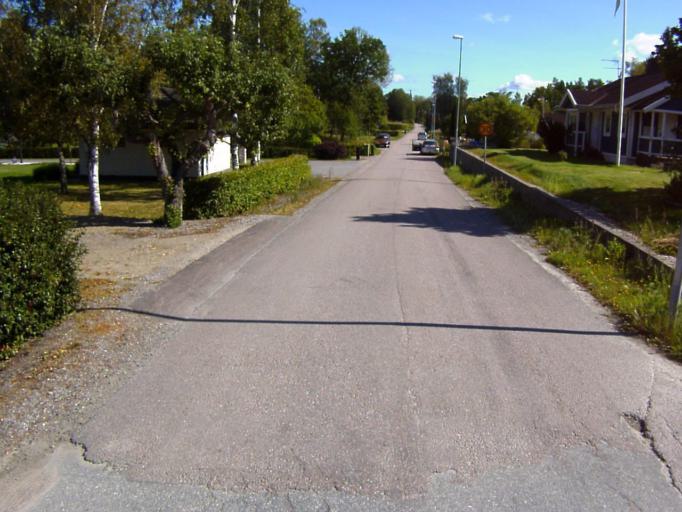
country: SE
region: Soedermanland
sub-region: Eskilstuna Kommun
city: Eskilstuna
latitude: 59.3500
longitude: 16.5591
